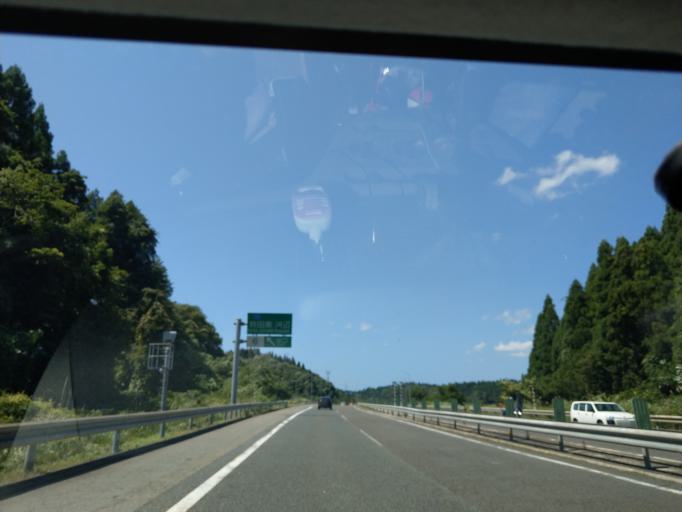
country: JP
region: Akita
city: Akita
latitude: 39.6569
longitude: 140.1960
